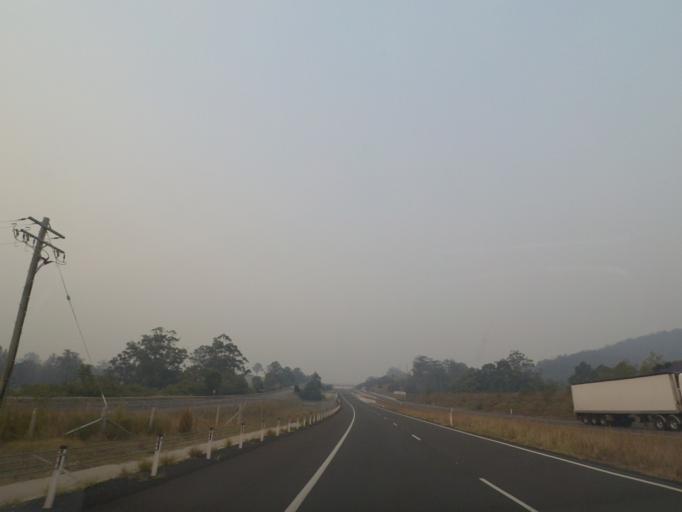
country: AU
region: New South Wales
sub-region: Nambucca Shire
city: Macksville
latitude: -30.7521
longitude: 152.9109
